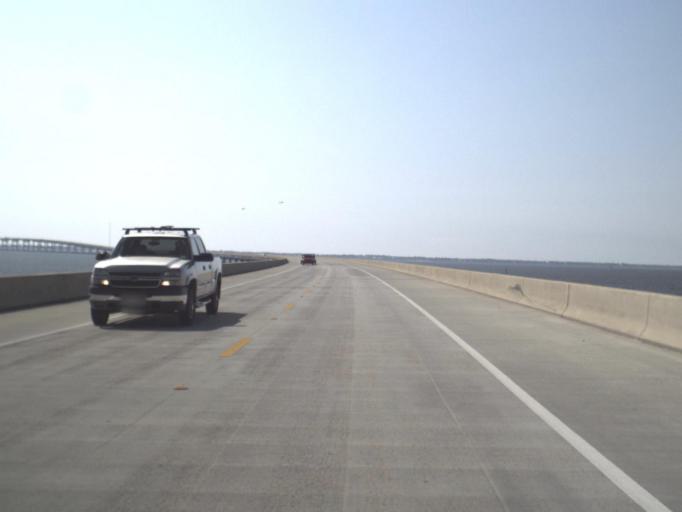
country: US
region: Florida
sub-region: Franklin County
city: Eastpoint
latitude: 29.7005
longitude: -84.8902
